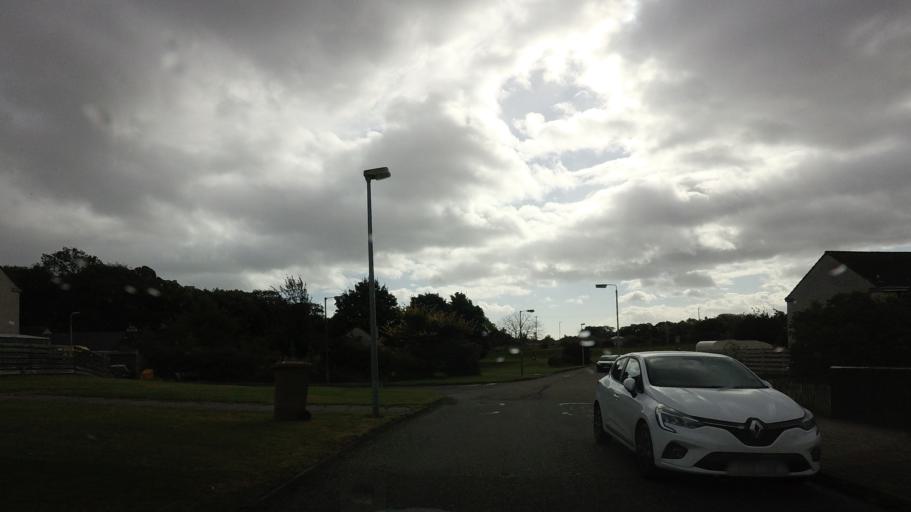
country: GB
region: Scotland
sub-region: Highland
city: Alness
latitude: 57.6945
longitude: -4.2686
